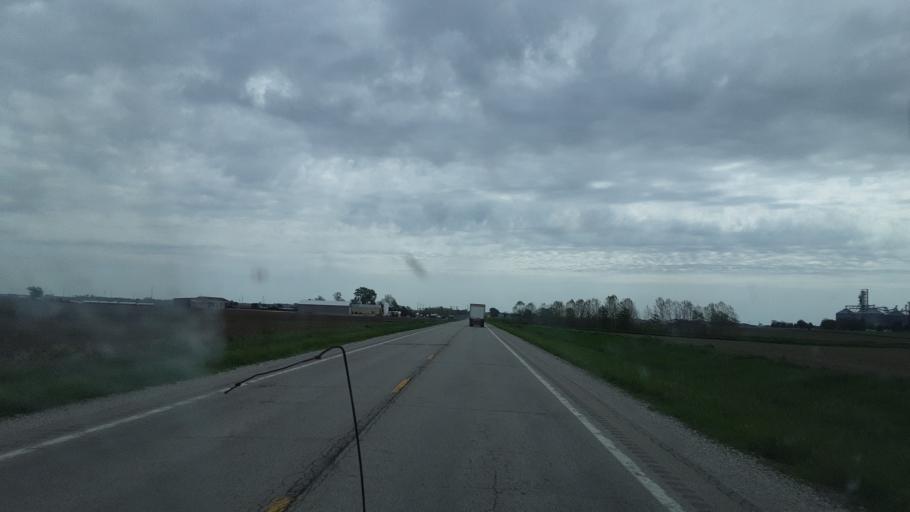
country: US
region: Illinois
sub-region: Tazewell County
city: Delavan
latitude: 40.3071
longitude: -89.5017
